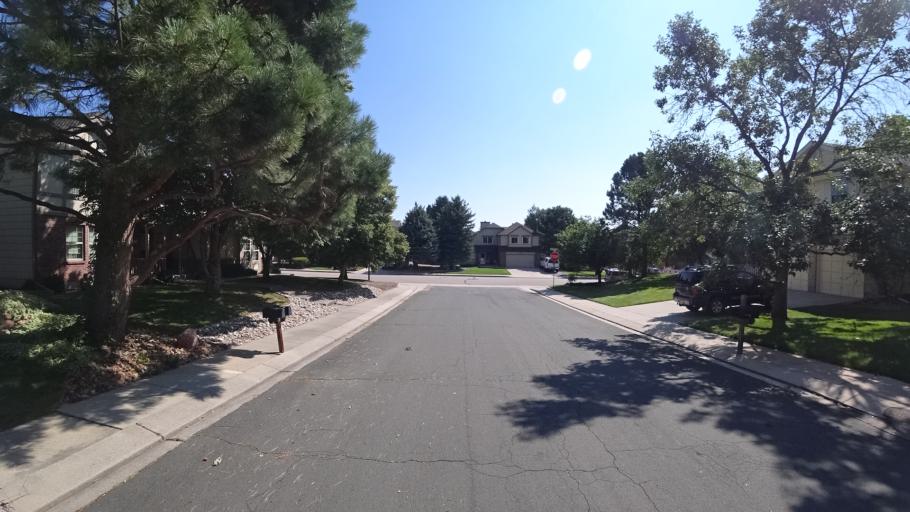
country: US
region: Colorado
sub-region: El Paso County
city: Air Force Academy
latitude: 38.9228
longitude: -104.8662
